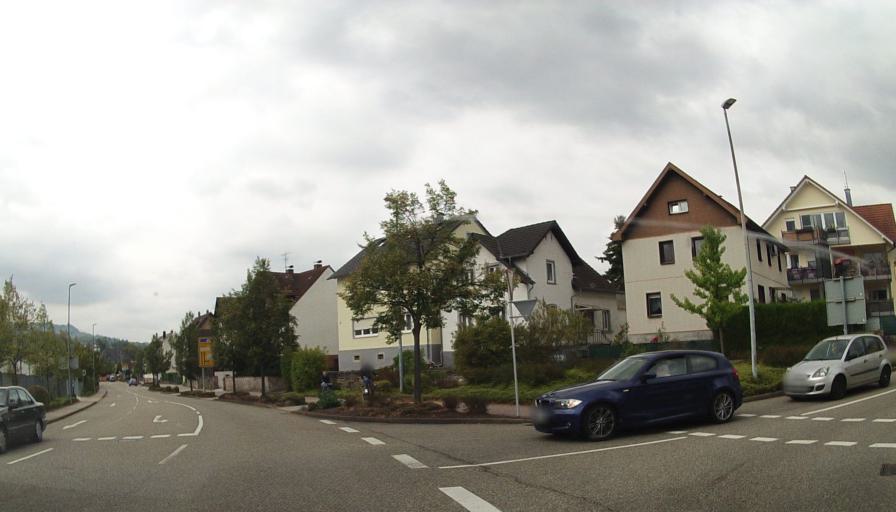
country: DE
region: Baden-Wuerttemberg
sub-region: Karlsruhe Region
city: Gaggenau
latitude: 48.8017
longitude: 8.3259
